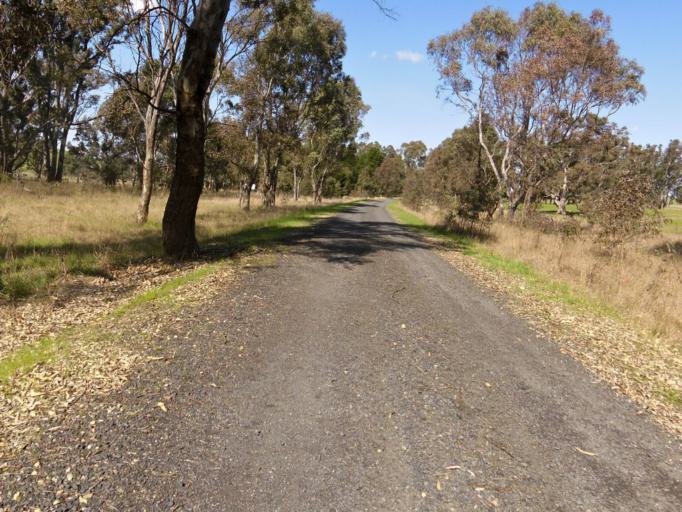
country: AU
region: Victoria
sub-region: Murrindindi
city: Alexandra
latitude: -36.9885
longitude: 145.7350
